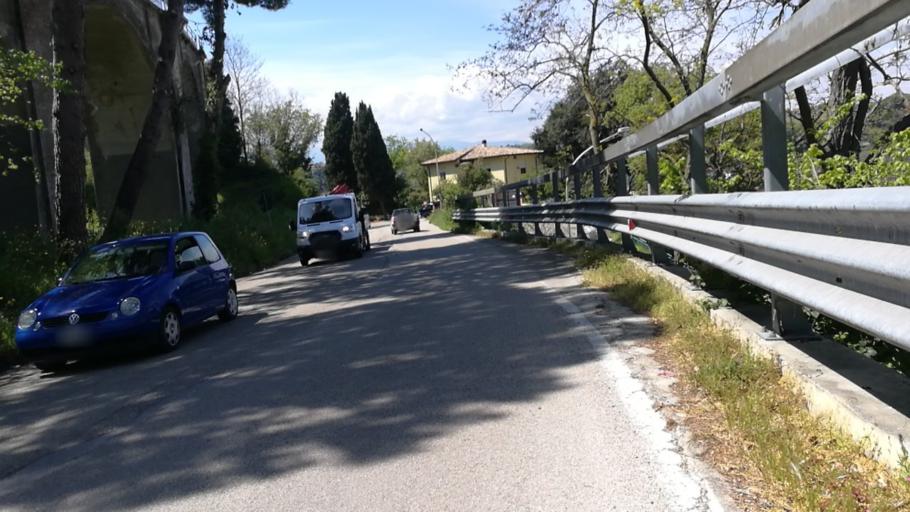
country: IT
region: Abruzzo
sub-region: Provincia di Chieti
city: Marina di San Vito
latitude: 42.3051
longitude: 14.4456
